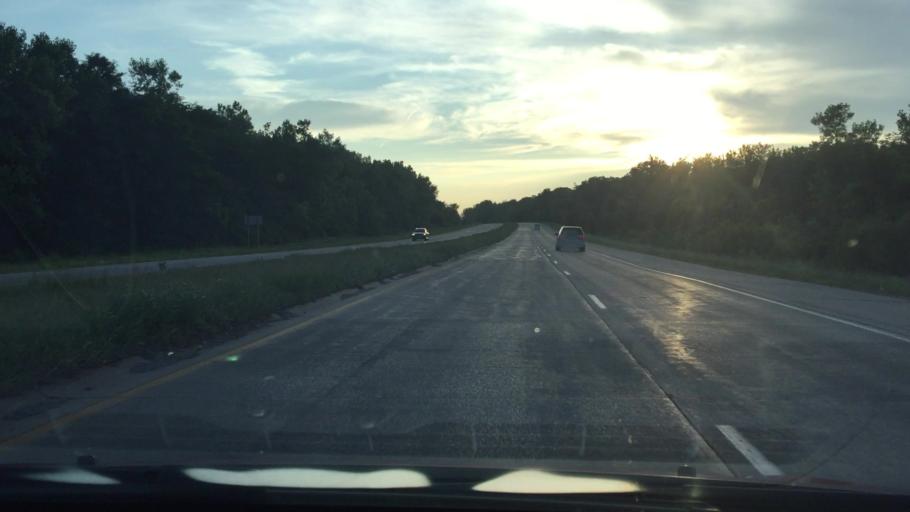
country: US
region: Iowa
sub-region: Muscatine County
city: Muscatine
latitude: 41.4524
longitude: -91.0467
